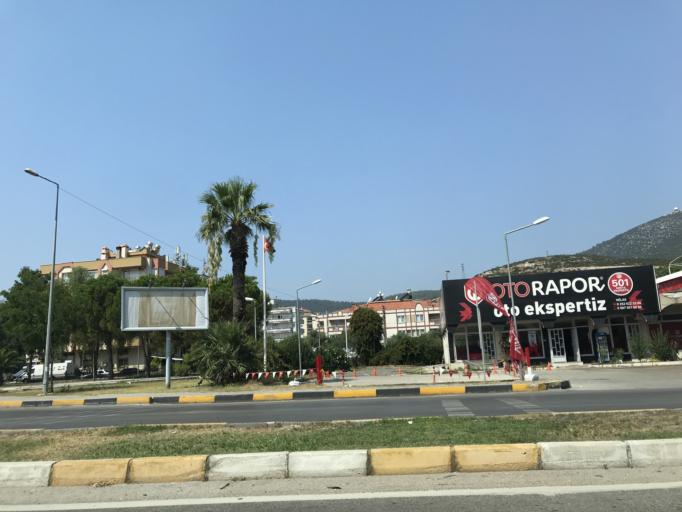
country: TR
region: Mugla
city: Milas
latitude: 37.2892
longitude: 27.7816
